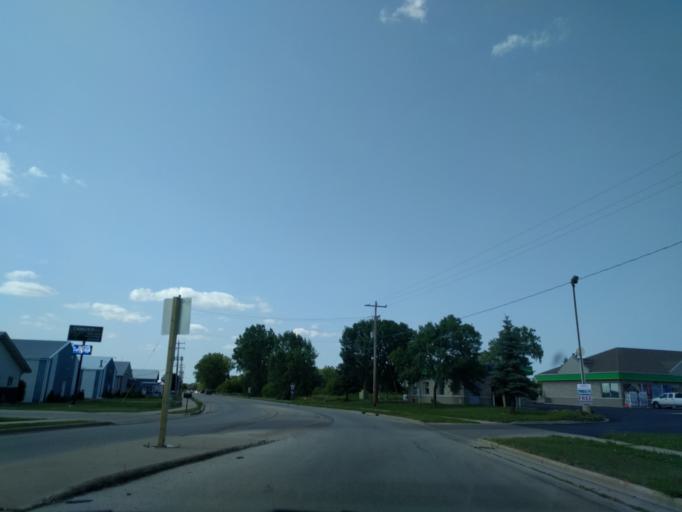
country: US
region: Wisconsin
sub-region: Brown County
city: Allouez
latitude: 44.4737
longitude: -87.9830
